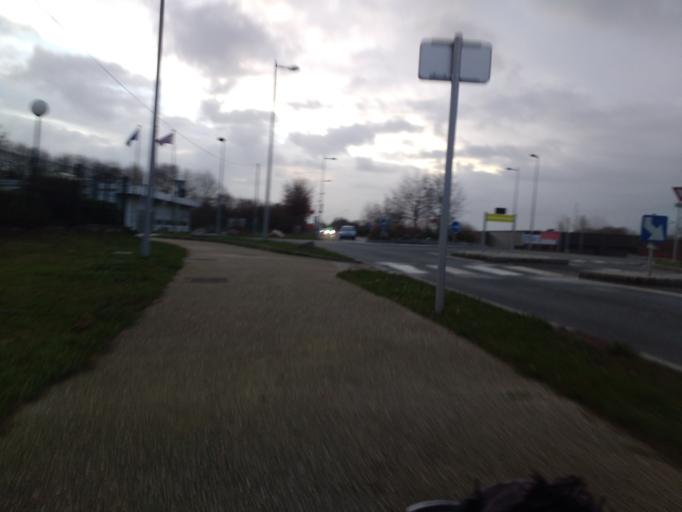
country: FR
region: Picardie
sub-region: Departement de la Somme
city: Longueau
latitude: 49.8654
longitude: 2.3710
